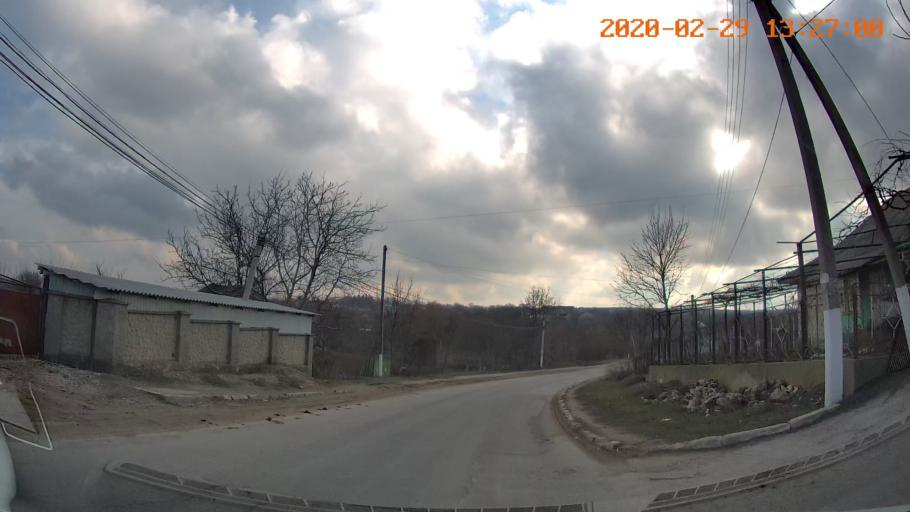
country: MD
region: Telenesti
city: Camenca
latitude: 47.9153
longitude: 28.6401
